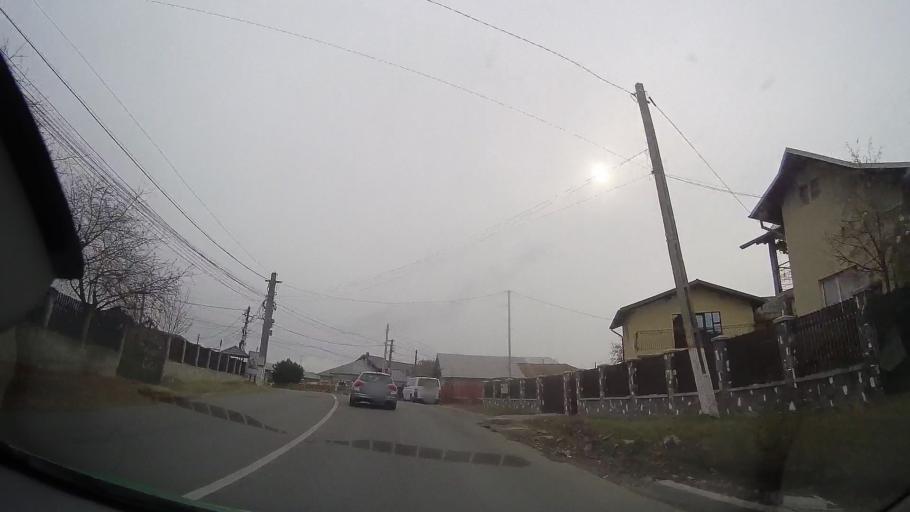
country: RO
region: Prahova
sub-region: Oras Baicoi
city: Tintea
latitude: 45.0319
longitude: 25.9045
